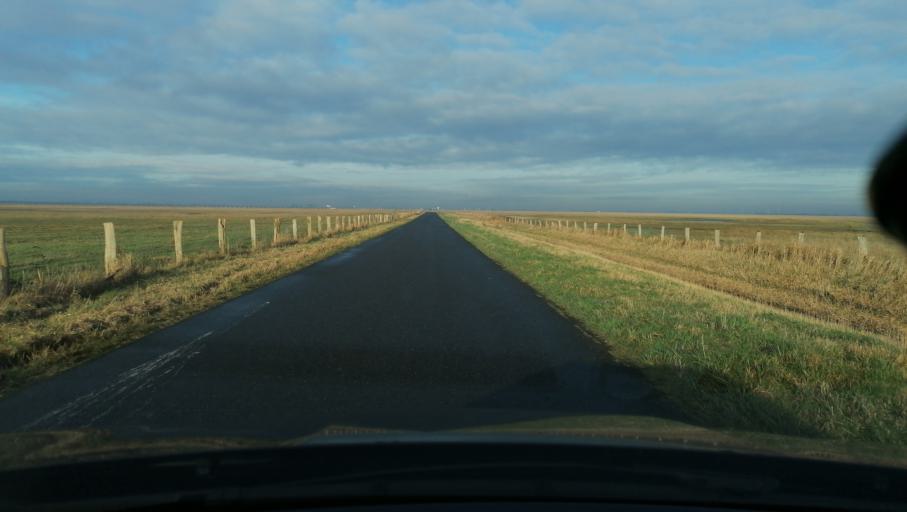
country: DE
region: Schleswig-Holstein
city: Friedrichsgabekoog
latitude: 54.1081
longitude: 8.9531
